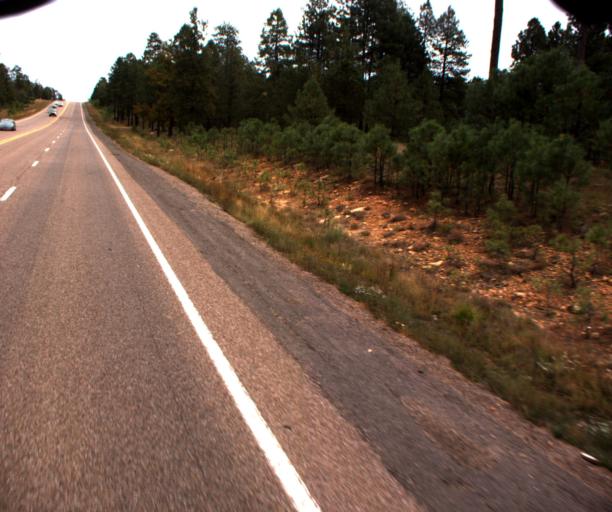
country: US
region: Arizona
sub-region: Navajo County
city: Heber-Overgaard
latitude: 34.3325
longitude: -110.7591
